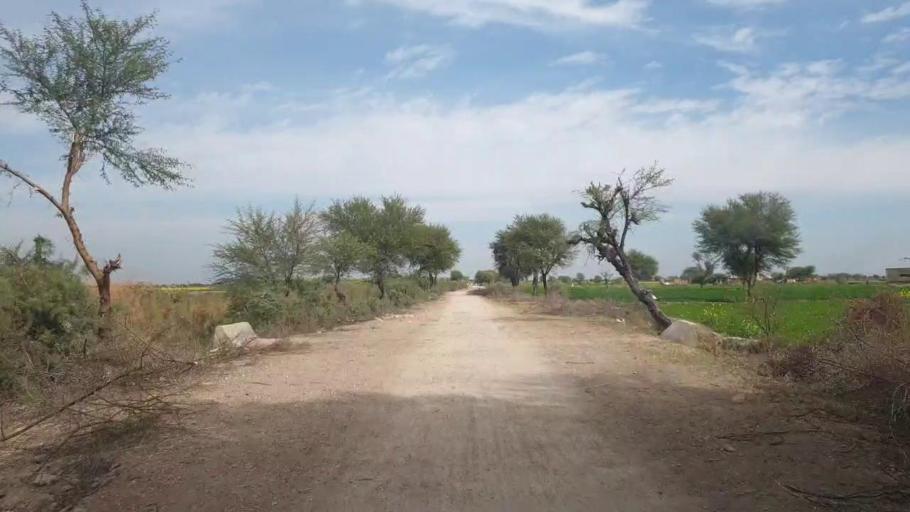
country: PK
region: Sindh
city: Sanghar
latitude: 26.0499
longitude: 68.9058
